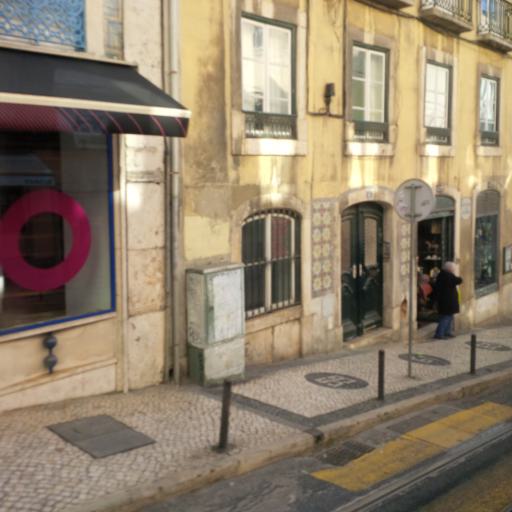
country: PT
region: Lisbon
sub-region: Lisbon
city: Lisbon
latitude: 38.7110
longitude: -9.1471
